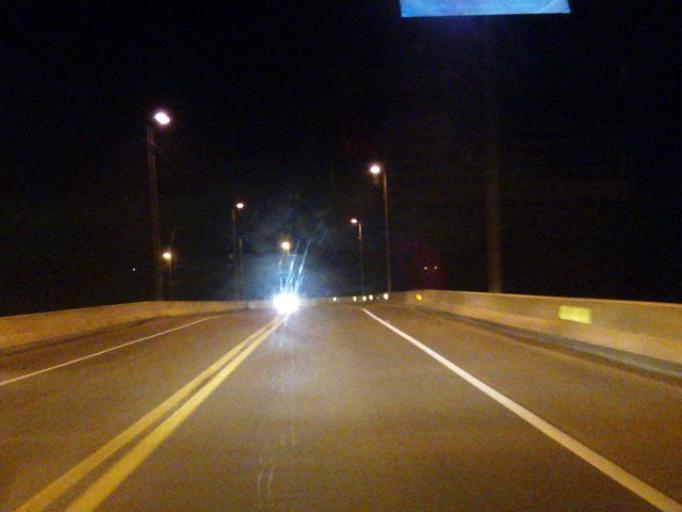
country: BR
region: Santa Catarina
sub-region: Itajai
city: Itajai
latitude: -26.9186
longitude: -48.7100
